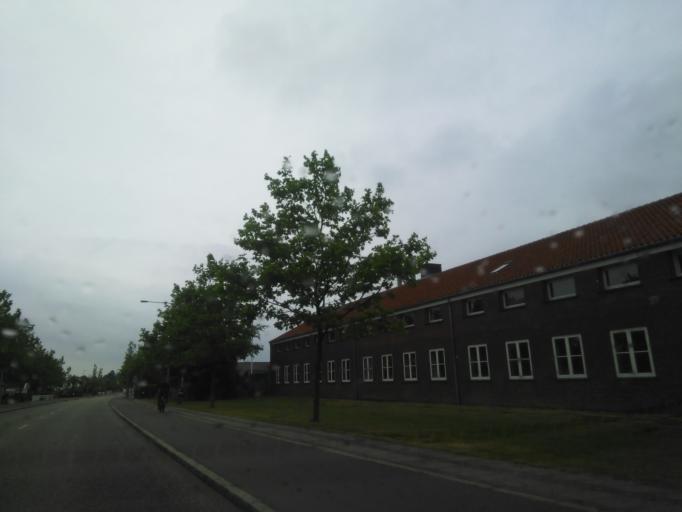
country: DK
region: Capital Region
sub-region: Bornholm Kommune
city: Ronne
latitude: 55.0931
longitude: 14.7270
